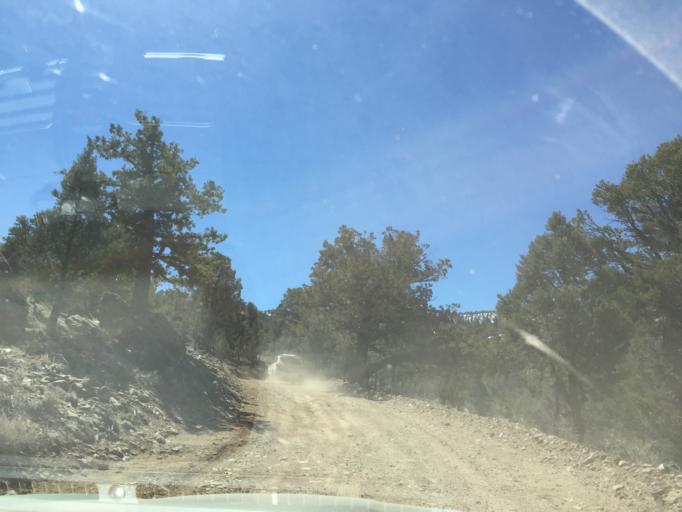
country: US
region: California
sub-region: San Bernardino County
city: Big Bear City
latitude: 34.2206
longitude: -116.7281
